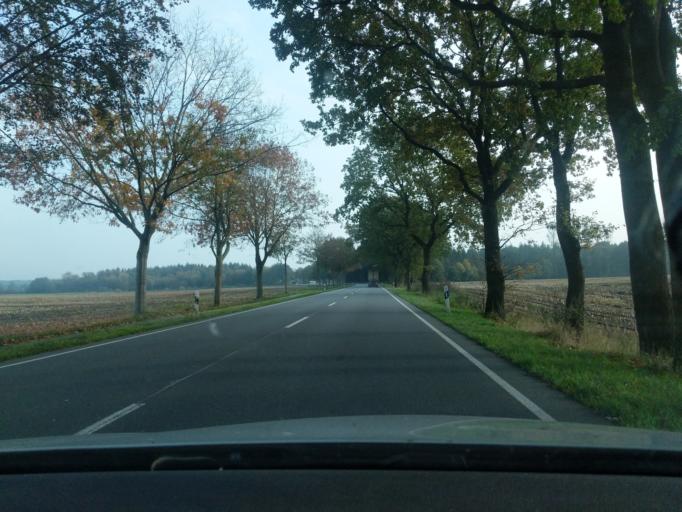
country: DE
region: Lower Saxony
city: Burweg
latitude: 53.6159
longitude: 9.2786
